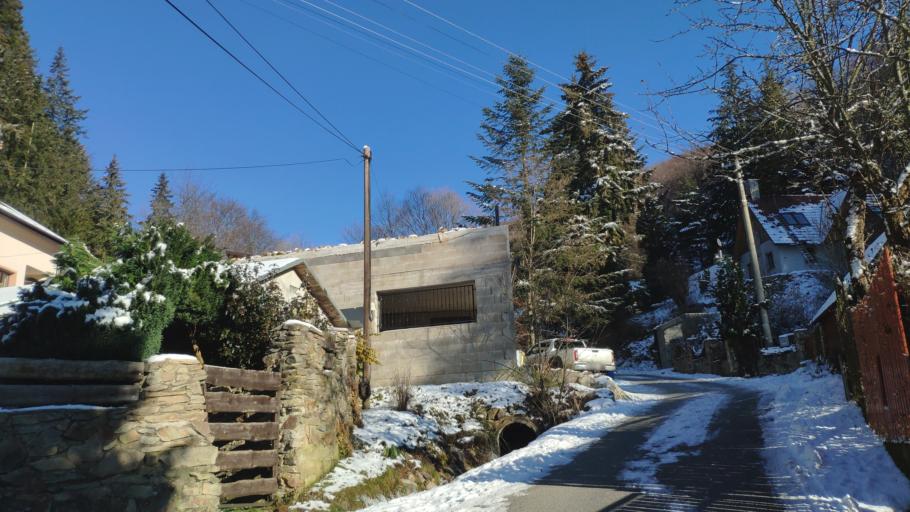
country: SK
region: Kosicky
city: Gelnica
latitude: 48.7560
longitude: 21.0049
